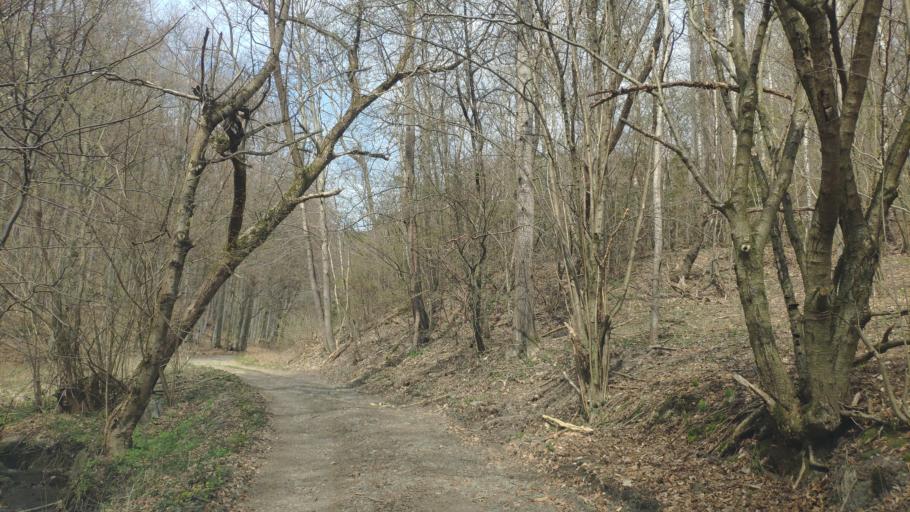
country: SK
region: Kosicky
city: Gelnica
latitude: 48.7506
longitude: 21.0275
